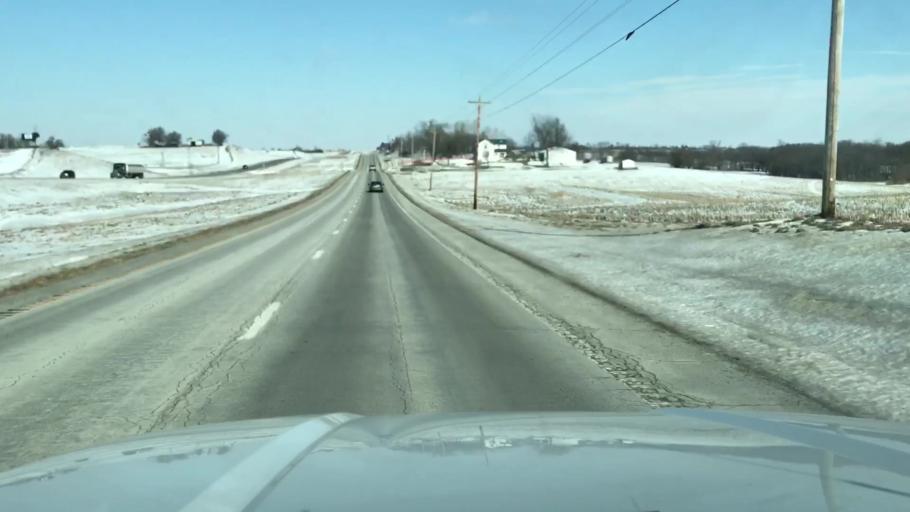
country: US
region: Missouri
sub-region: Andrew County
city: Savannah
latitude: 40.0072
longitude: -94.8796
